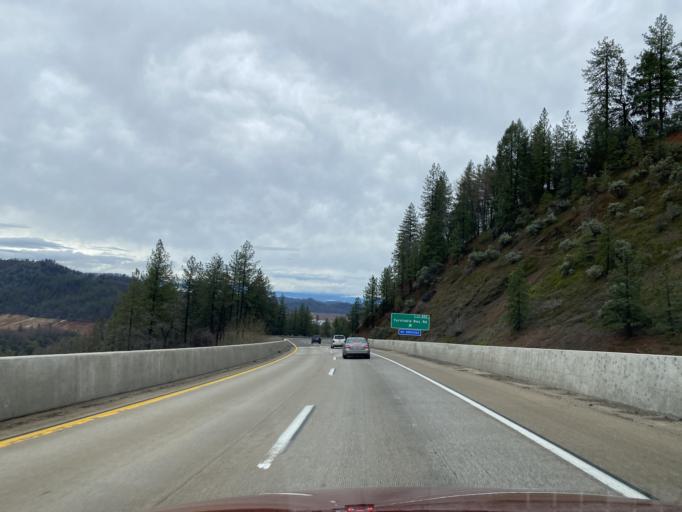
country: US
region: California
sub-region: Shasta County
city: Shasta Lake
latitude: 40.7773
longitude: -122.3184
